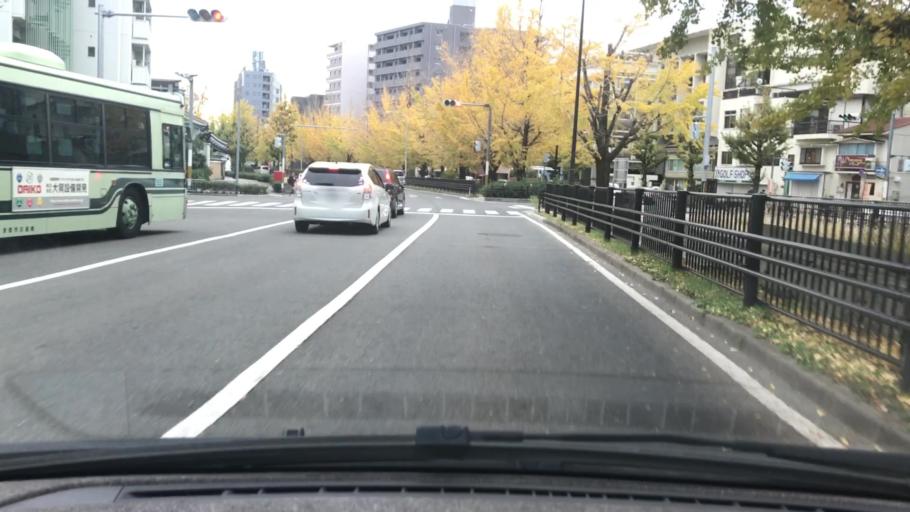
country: JP
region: Kyoto
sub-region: Kyoto-shi
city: Kamigyo-ku
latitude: 35.0362
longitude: 135.7515
